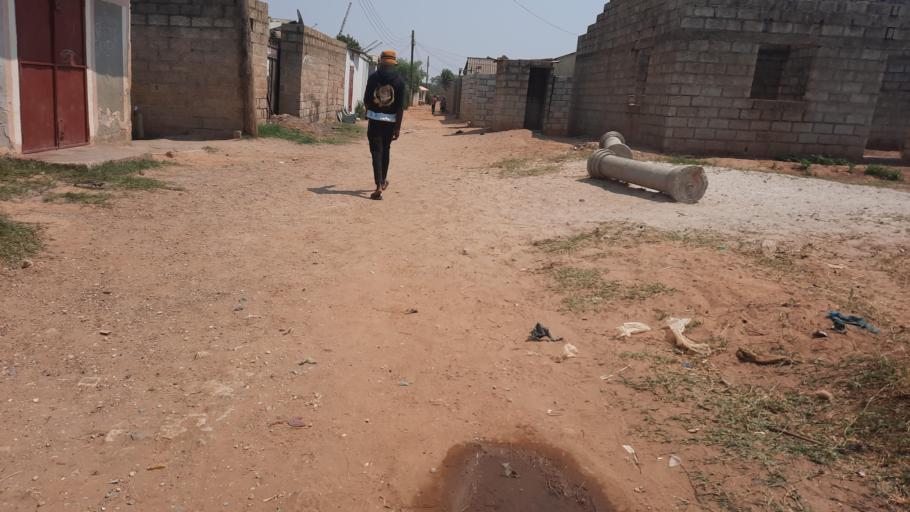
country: ZM
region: Lusaka
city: Lusaka
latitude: -15.3943
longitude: 28.3811
